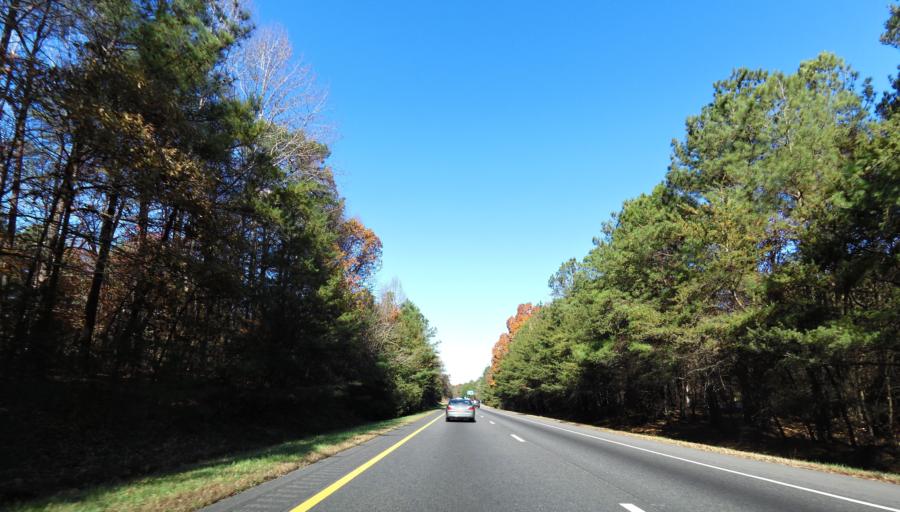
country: US
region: Virginia
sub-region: James City County
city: Williamsburg
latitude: 37.3788
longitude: -76.7567
